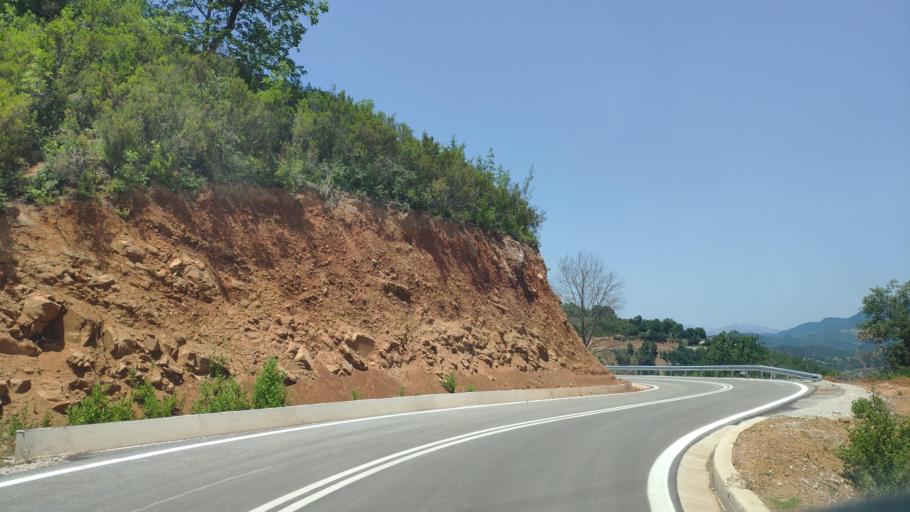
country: GR
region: Epirus
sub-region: Nomos Artas
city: Ano Kalentini
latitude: 39.1868
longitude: 21.3558
